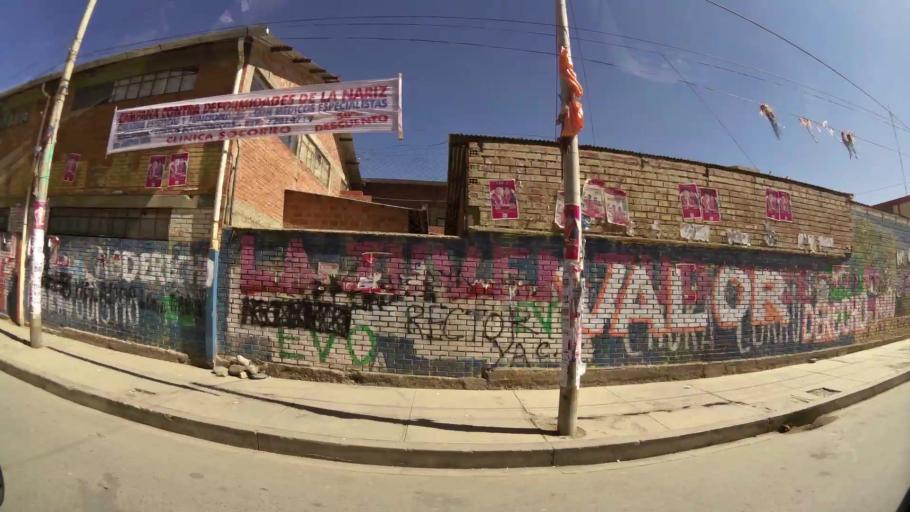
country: BO
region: La Paz
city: La Paz
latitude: -16.4926
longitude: -68.1935
